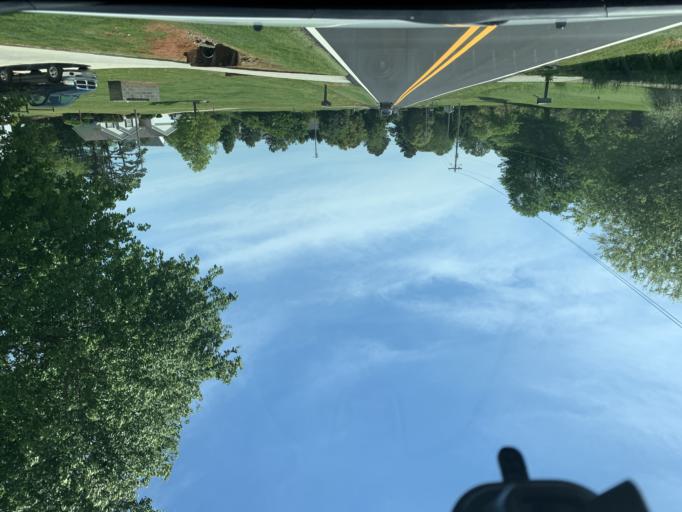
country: US
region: Georgia
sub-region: Forsyth County
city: Cumming
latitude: 34.2605
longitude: -84.0307
